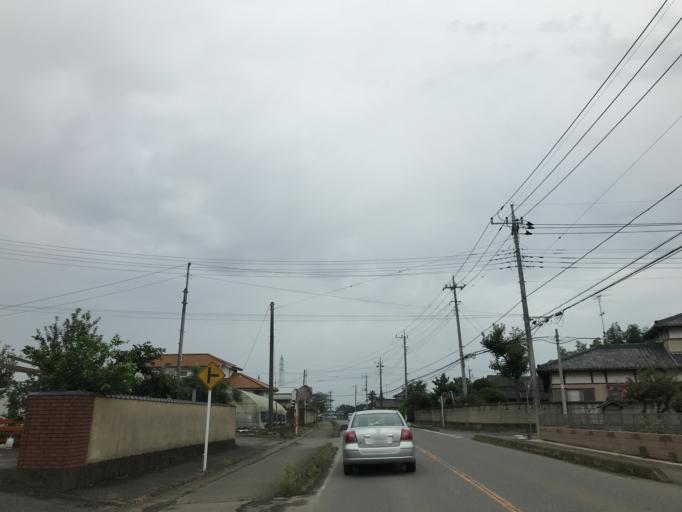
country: JP
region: Ibaraki
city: Sakai
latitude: 36.1488
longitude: 139.7936
